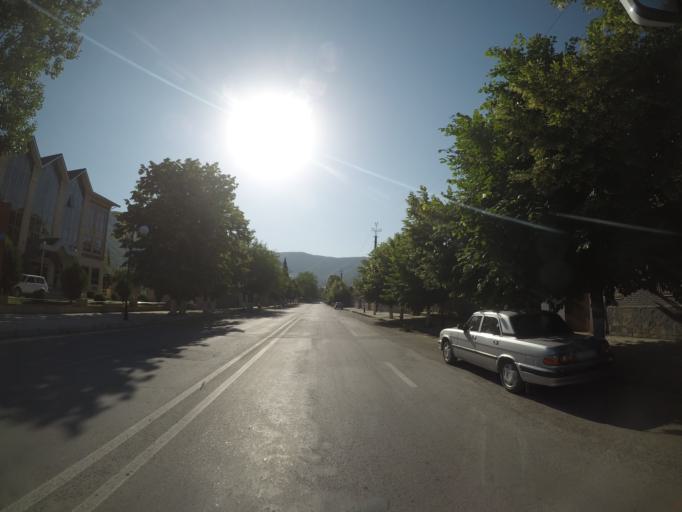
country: AZ
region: Shaki City
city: Sheki
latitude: 41.2062
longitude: 47.1701
